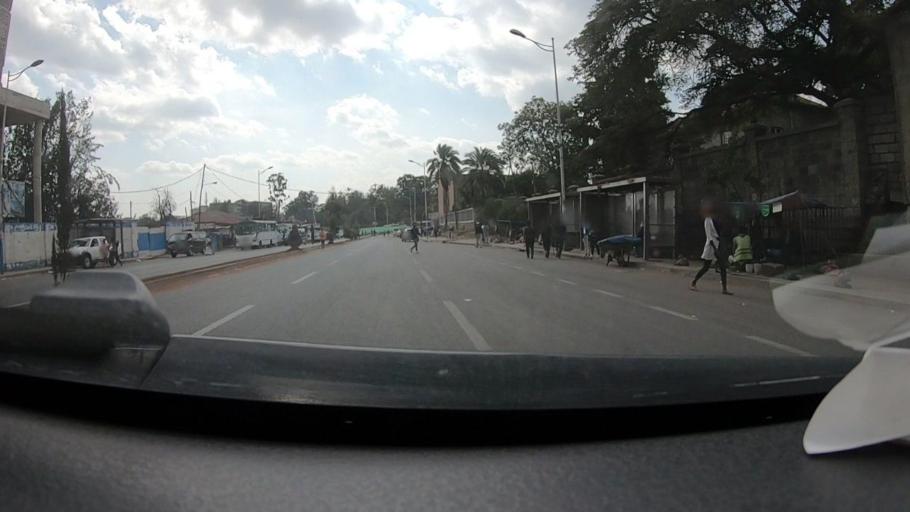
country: ET
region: Adis Abeba
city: Addis Ababa
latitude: 9.0442
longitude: 38.7639
